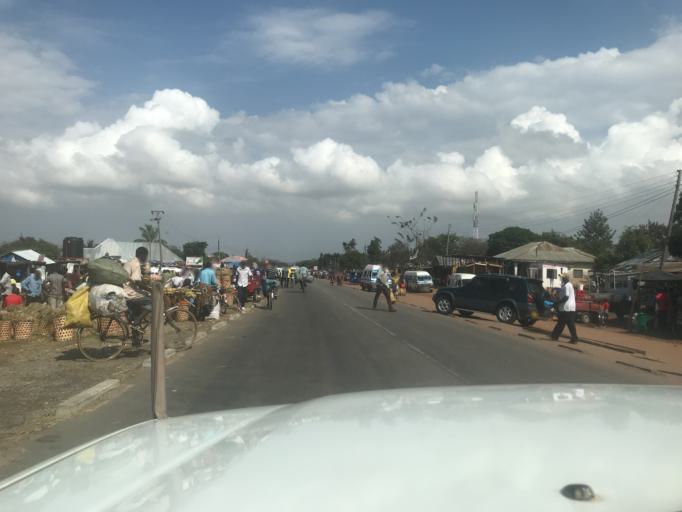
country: TZ
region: Mwanza
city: Usagara
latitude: -2.5554
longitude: 33.0488
